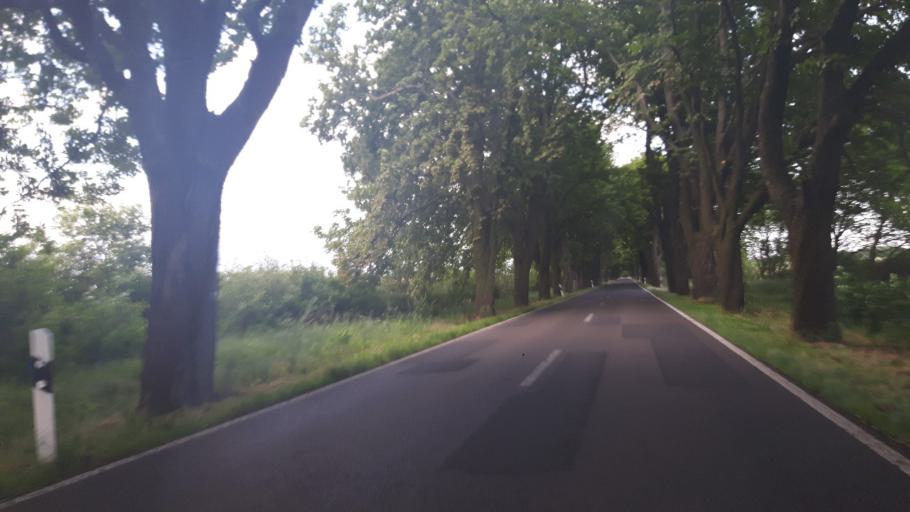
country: DE
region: Brandenburg
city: Melchow
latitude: 52.7527
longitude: 13.7648
